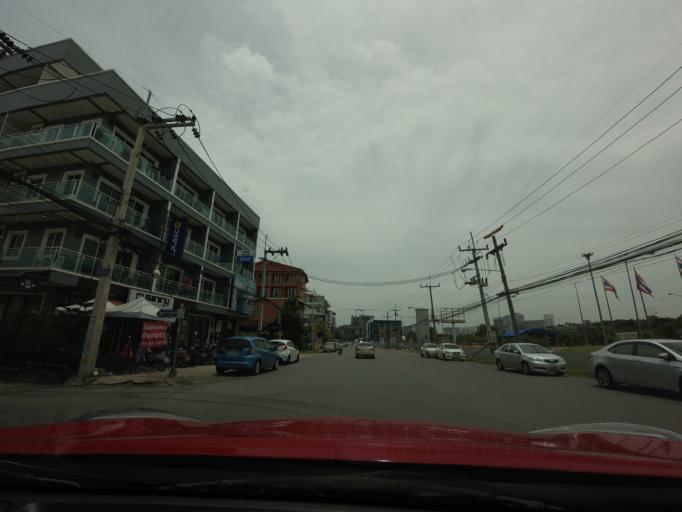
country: TH
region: Songkhla
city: Hat Yai
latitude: 7.0007
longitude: 100.5041
